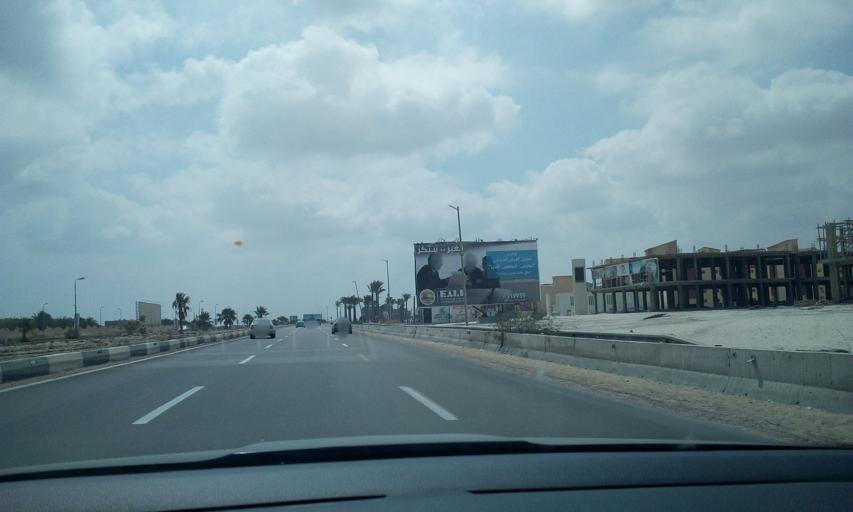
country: EG
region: Muhafazat Matruh
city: Al `Alamayn
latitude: 30.8304
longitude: 28.9693
